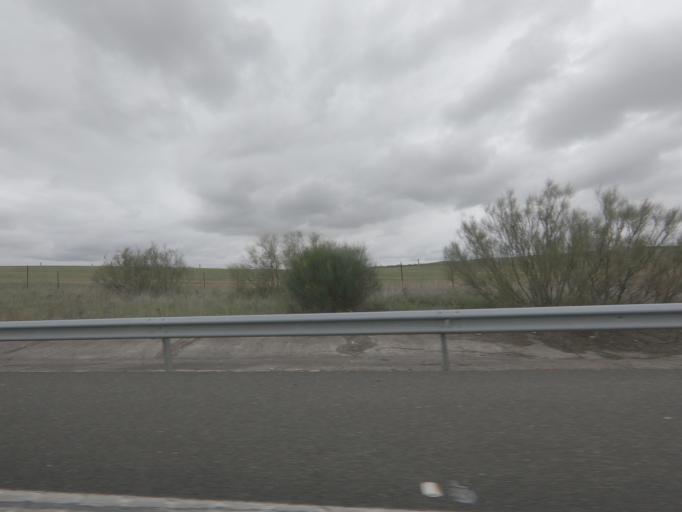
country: ES
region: Extremadura
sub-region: Provincia de Caceres
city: Galisteo
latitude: 39.9411
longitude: -6.2028
